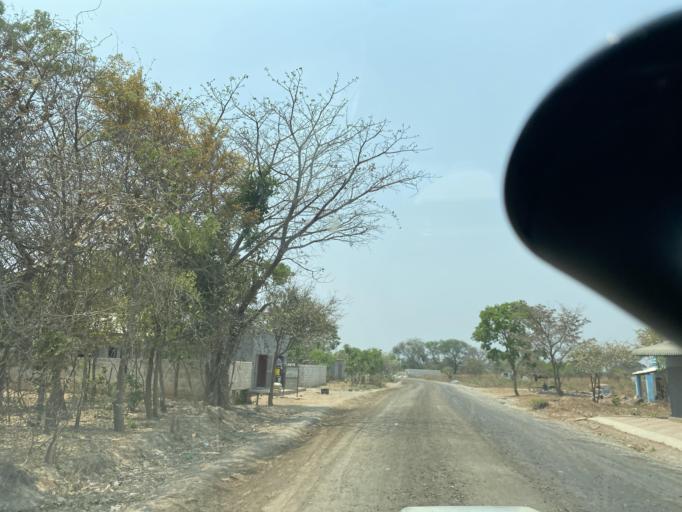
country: ZM
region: Lusaka
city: Lusaka
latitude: -15.5578
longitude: 28.4391
